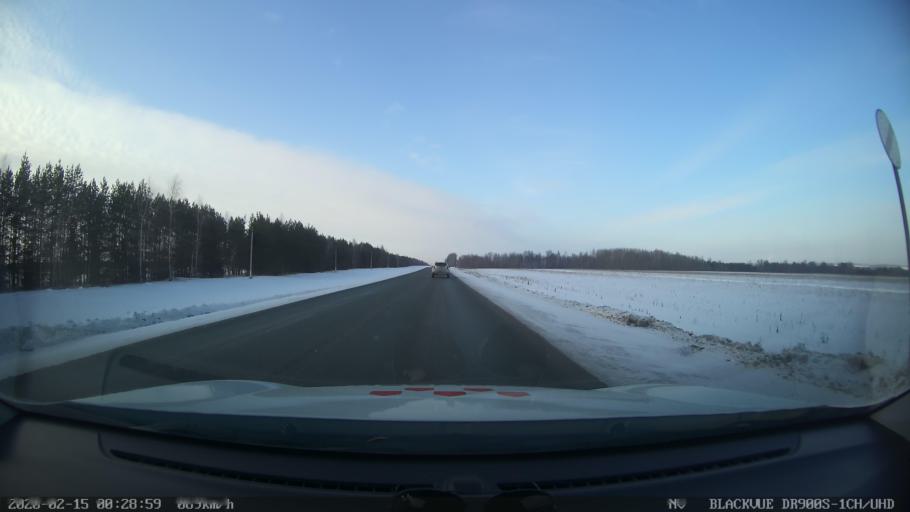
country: RU
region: Tatarstan
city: Verkhniy Uslon
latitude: 55.6467
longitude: 48.8735
